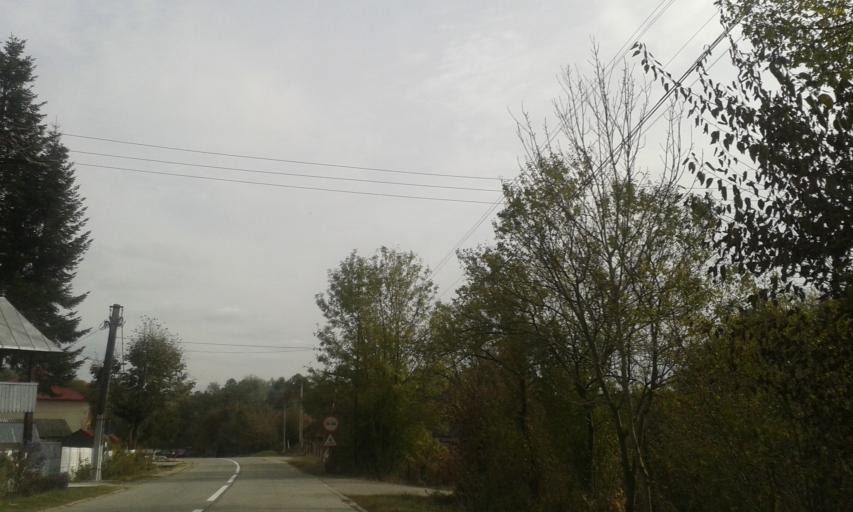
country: RO
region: Valcea
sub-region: Comuna Gradistea
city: Gradistea
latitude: 44.9098
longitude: 23.7884
